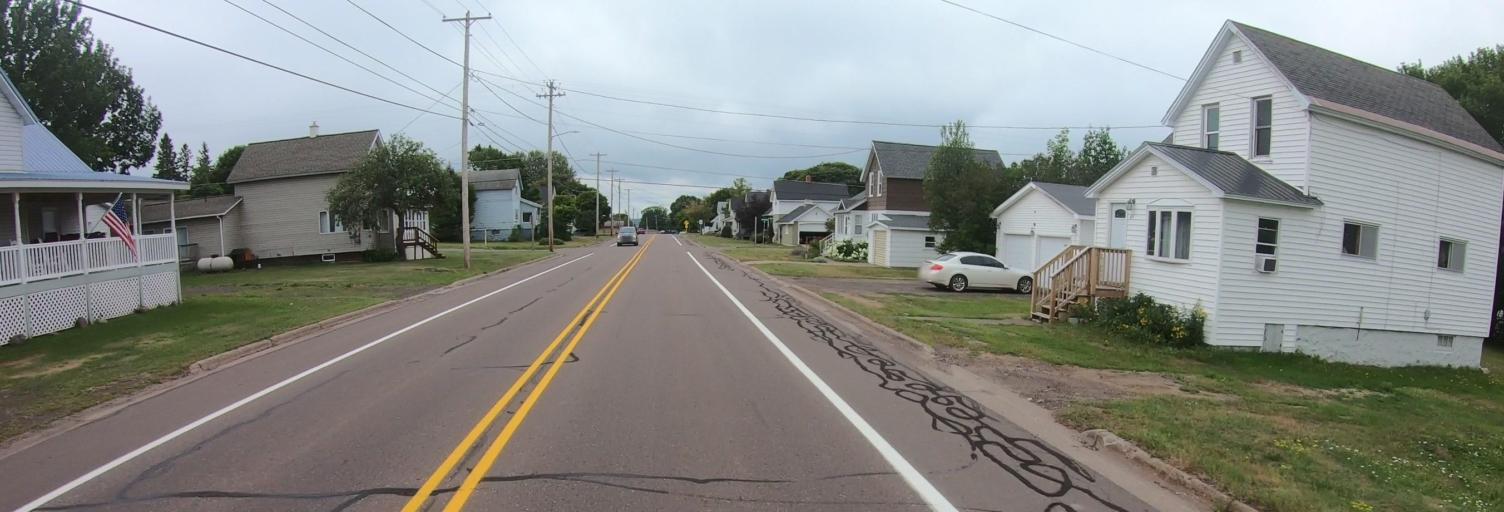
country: US
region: Michigan
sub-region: Houghton County
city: Laurium
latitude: 47.3062
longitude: -88.3614
